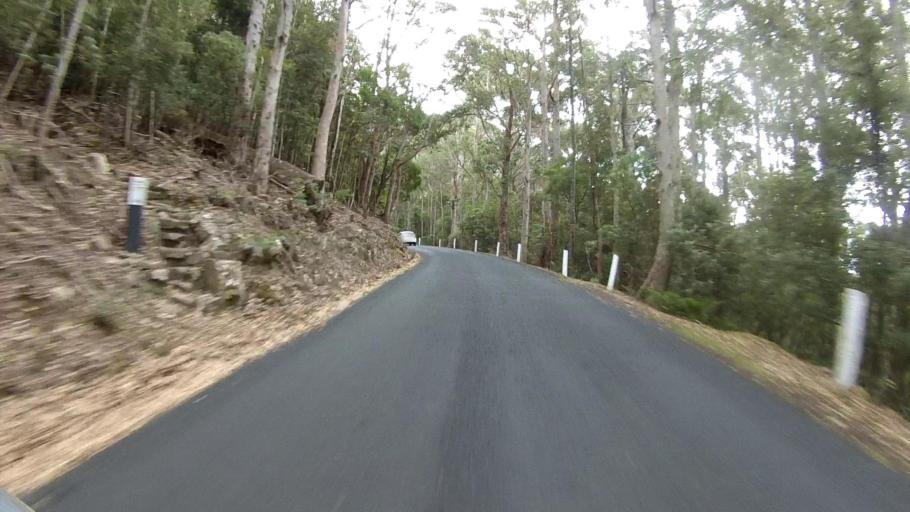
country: AU
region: Tasmania
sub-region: Hobart
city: Dynnyrne
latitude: -42.9127
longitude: 147.2577
